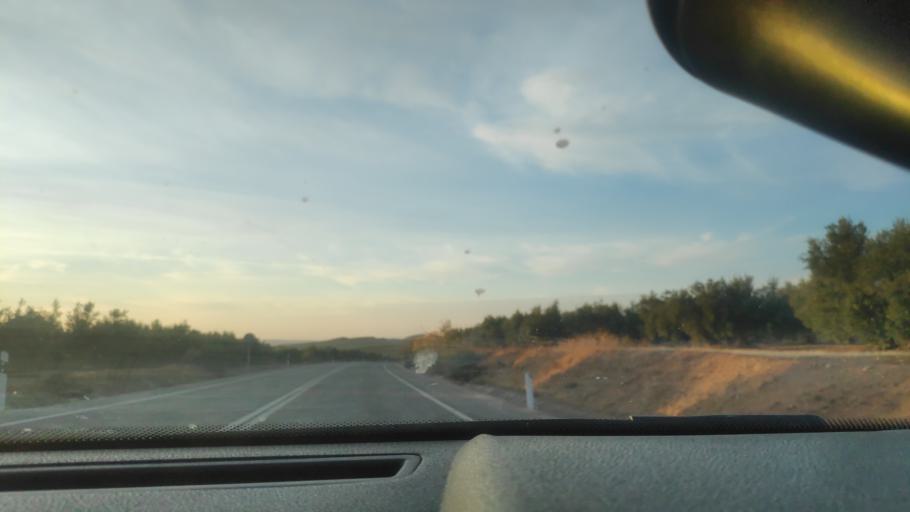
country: ES
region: Andalusia
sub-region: Provincia de Jaen
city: Torredonjimeno
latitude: 37.7838
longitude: -3.9843
